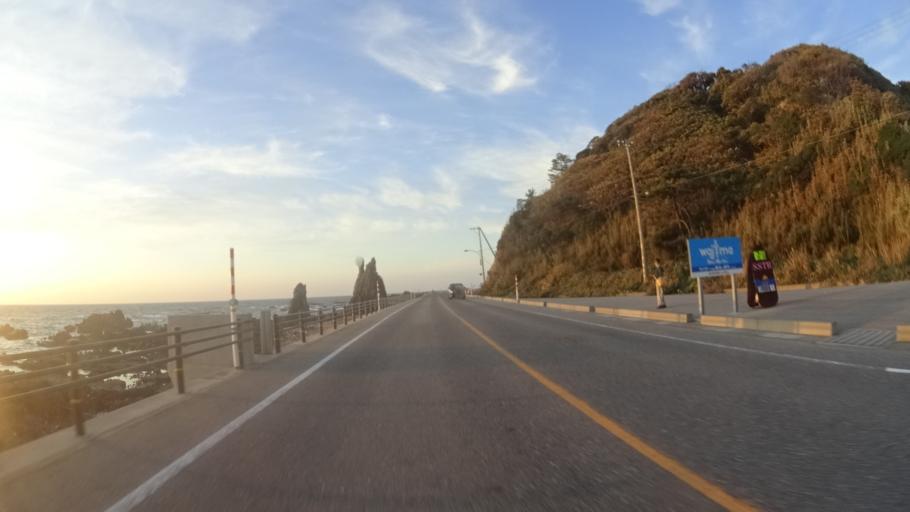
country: JP
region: Ishikawa
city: Nanao
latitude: 37.2356
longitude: 136.7017
